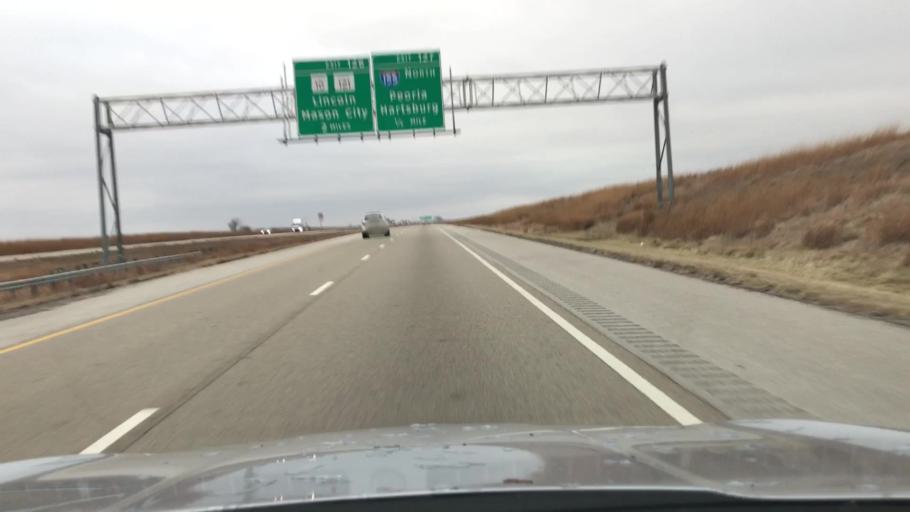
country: US
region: Illinois
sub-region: Logan County
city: Lincoln
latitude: 40.1817
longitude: -89.3942
